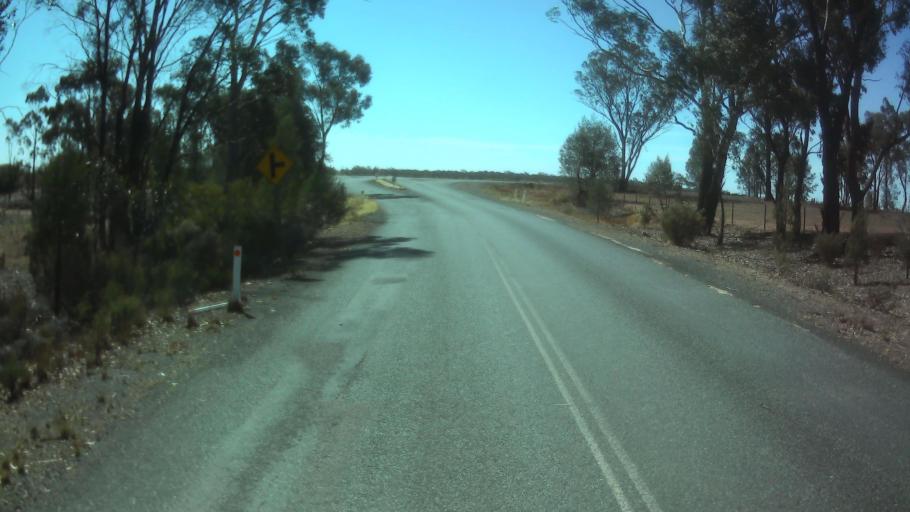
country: AU
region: New South Wales
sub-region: Weddin
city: Grenfell
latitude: -33.7571
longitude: 147.8559
